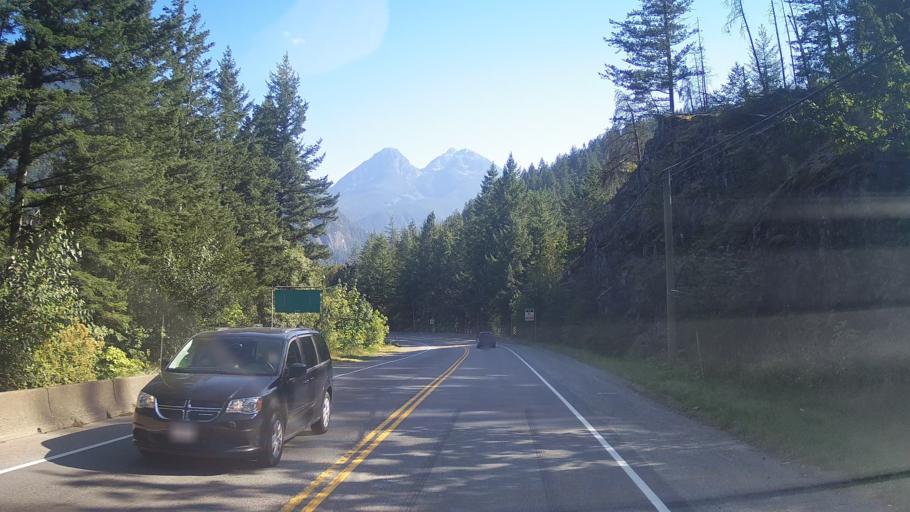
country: CA
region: British Columbia
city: Hope
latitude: 49.3897
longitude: -121.4612
